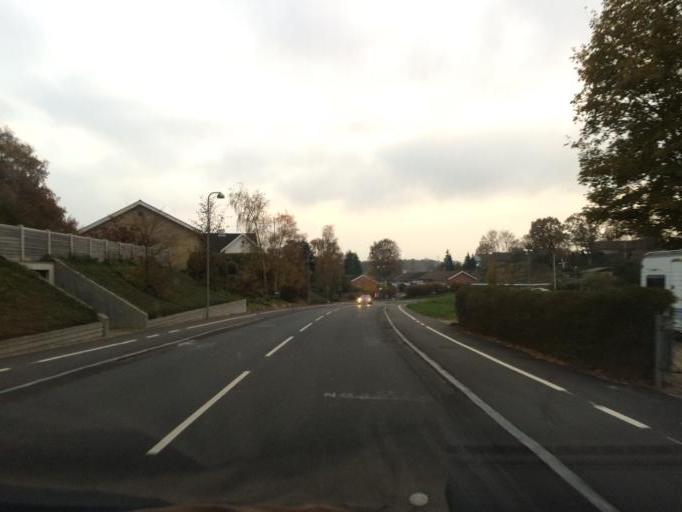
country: DK
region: Central Jutland
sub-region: Silkeborg Kommune
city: Silkeborg
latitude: 56.1802
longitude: 9.5202
